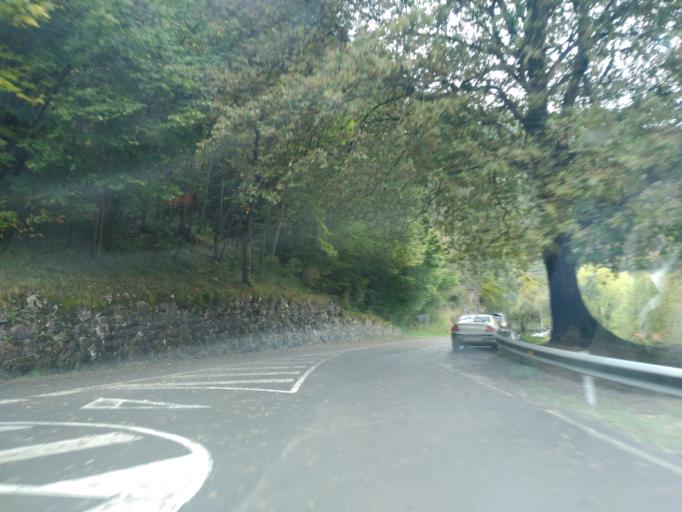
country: ES
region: Cantabria
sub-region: Provincia de Cantabria
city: Puente Viesgo
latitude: 43.2926
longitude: -3.9687
